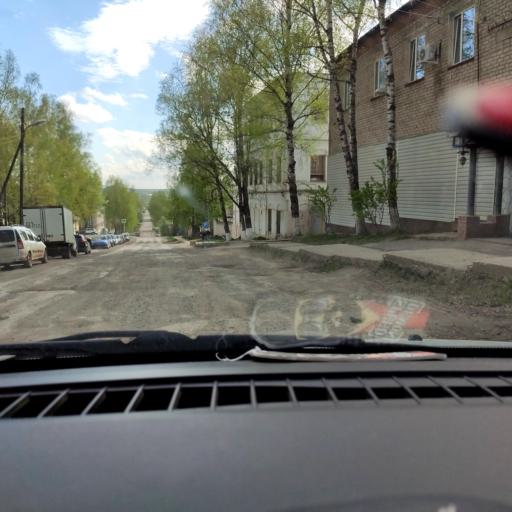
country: RU
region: Perm
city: Kudymkar
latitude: 59.0128
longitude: 54.6531
